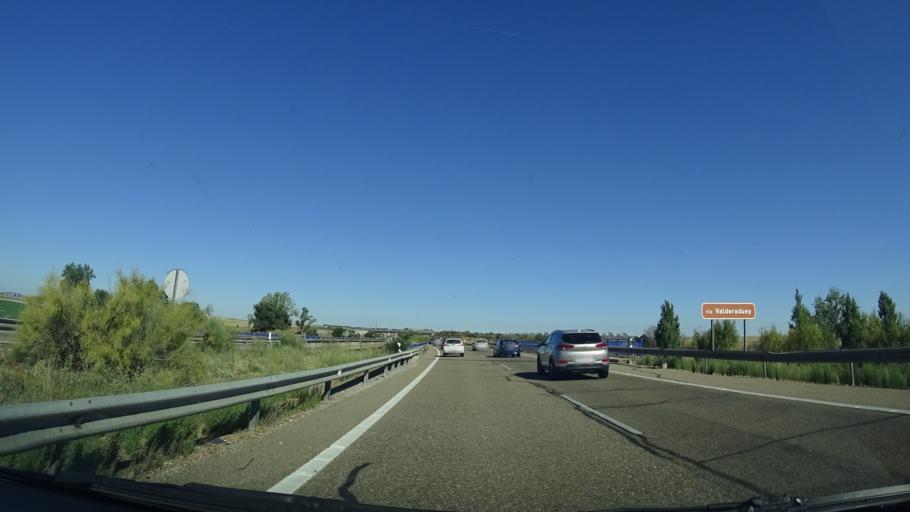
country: ES
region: Castille and Leon
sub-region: Provincia de Zamora
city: Villalpando
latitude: 41.8678
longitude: -5.4322
